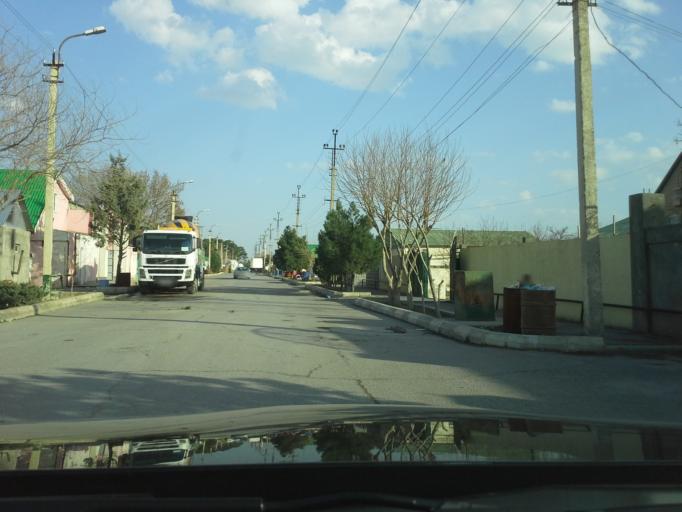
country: TM
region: Ahal
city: Abadan
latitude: 38.0264
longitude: 58.2361
